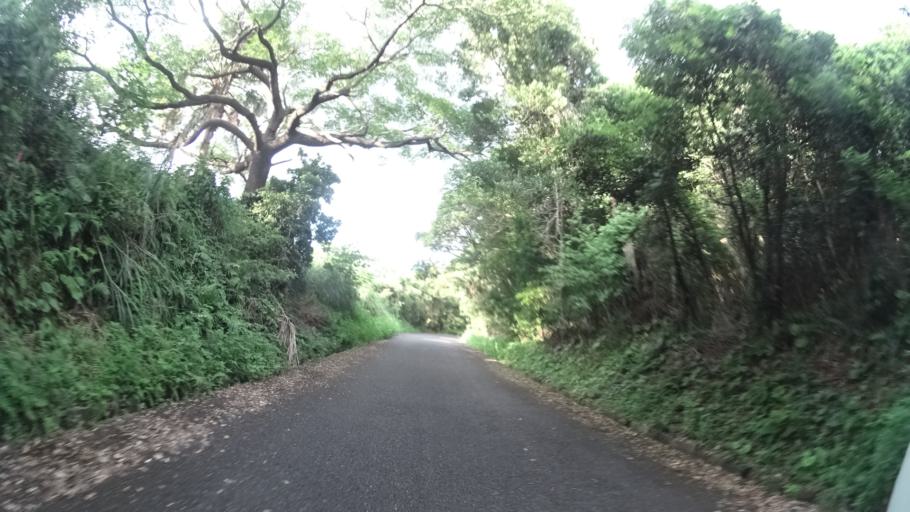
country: JP
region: Kagoshima
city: Nishinoomote
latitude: 30.2322
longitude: 130.4854
